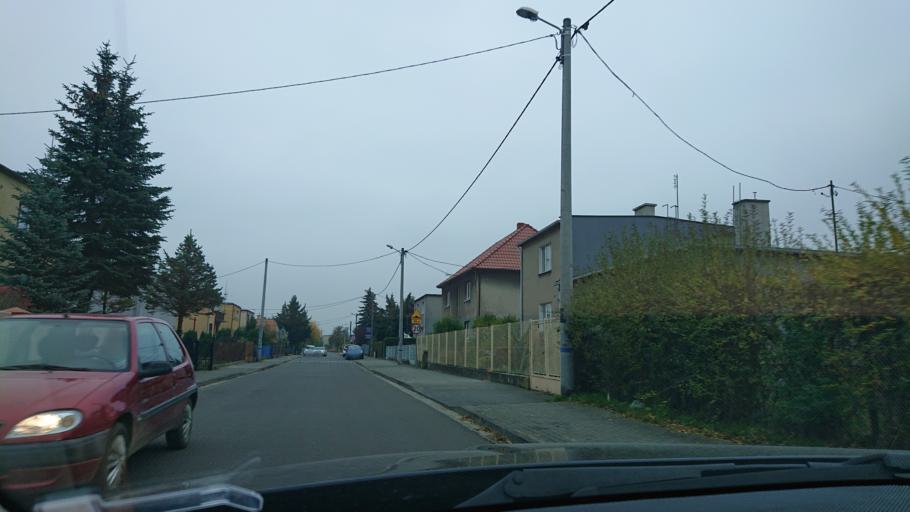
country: PL
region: Greater Poland Voivodeship
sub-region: Powiat gnieznienski
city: Gniezno
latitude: 52.5388
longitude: 17.6238
